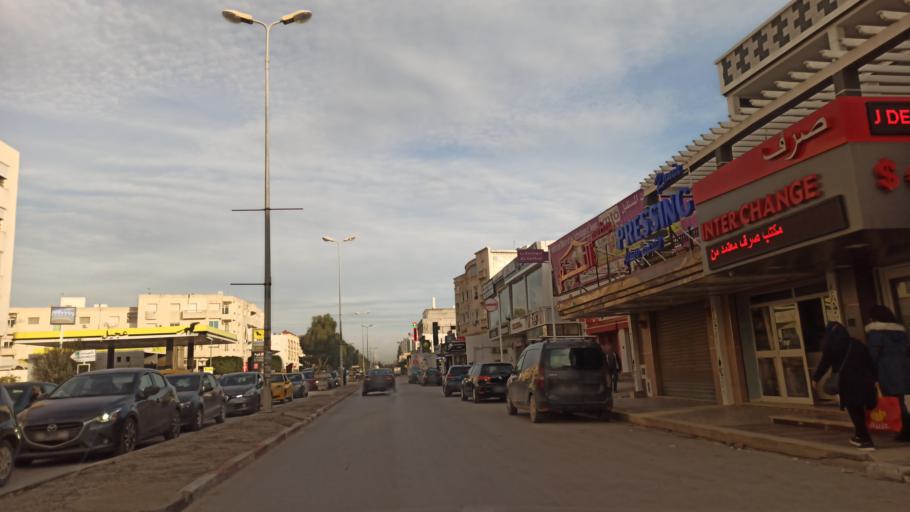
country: TN
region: Tunis
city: La Goulette
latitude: 36.8539
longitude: 10.2576
